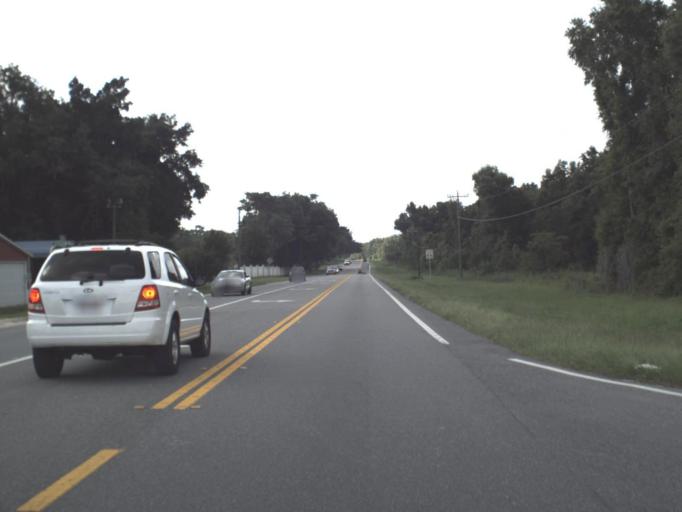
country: US
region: Florida
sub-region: Citrus County
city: Inverness Highlands North
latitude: 28.8777
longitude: -82.3635
